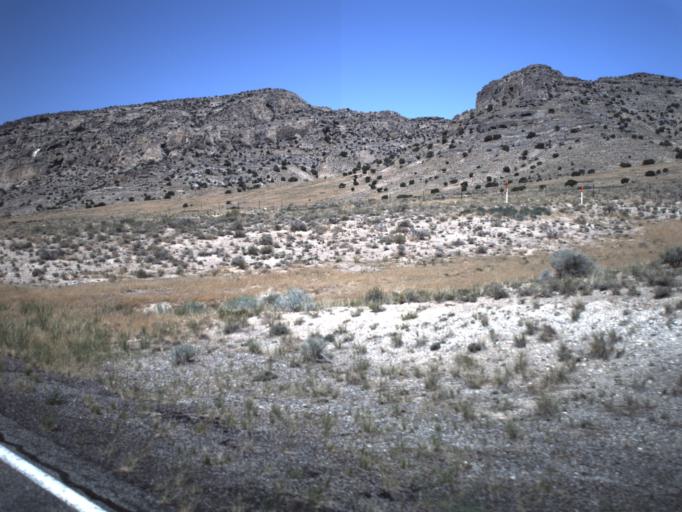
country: US
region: Utah
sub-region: Beaver County
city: Milford
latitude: 39.0734
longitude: -113.6420
